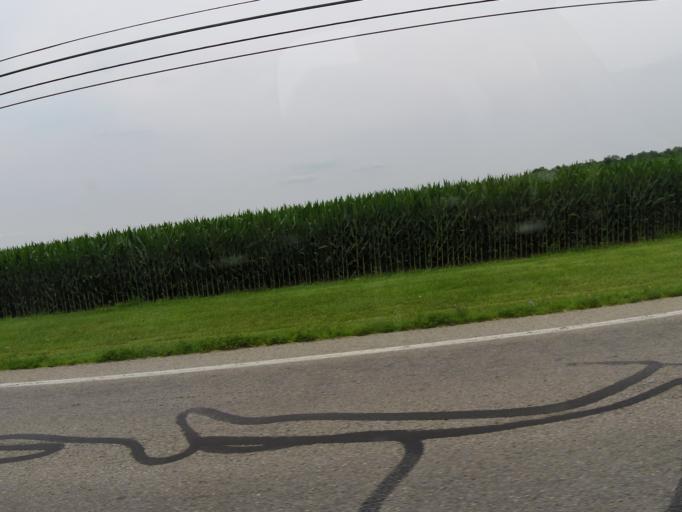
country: US
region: Ohio
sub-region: Clinton County
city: Wilmington
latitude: 39.4839
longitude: -83.9319
